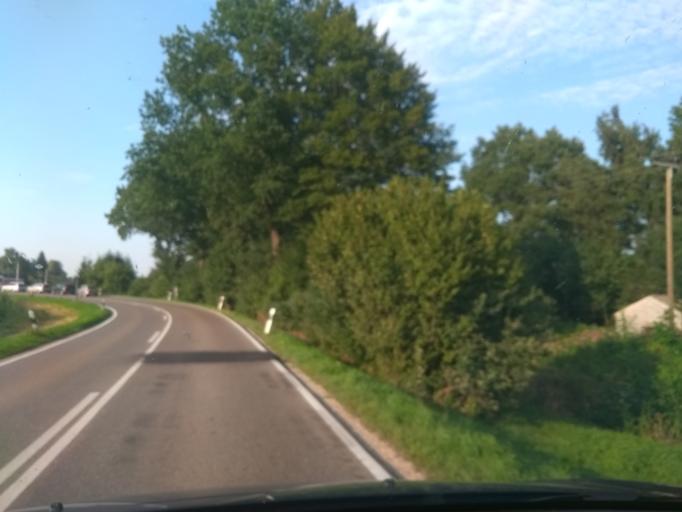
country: DE
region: Bavaria
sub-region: Upper Bavaria
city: Schwabhausen
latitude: 48.3155
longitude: 11.3883
